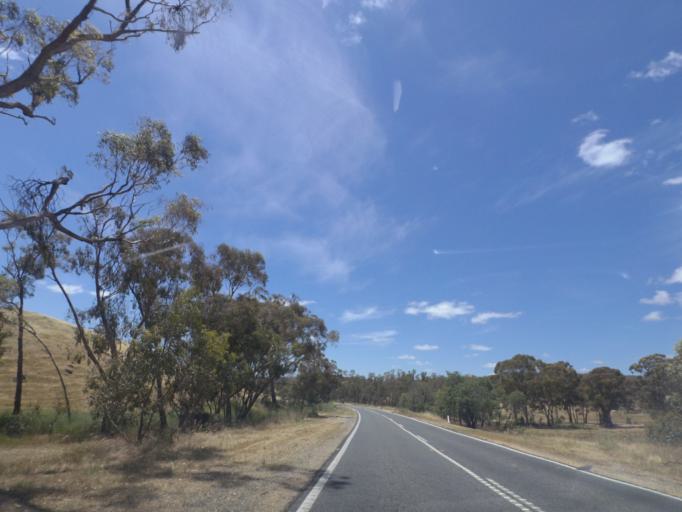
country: AU
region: Victoria
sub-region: Mount Alexander
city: Castlemaine
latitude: -37.2013
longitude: 144.1442
